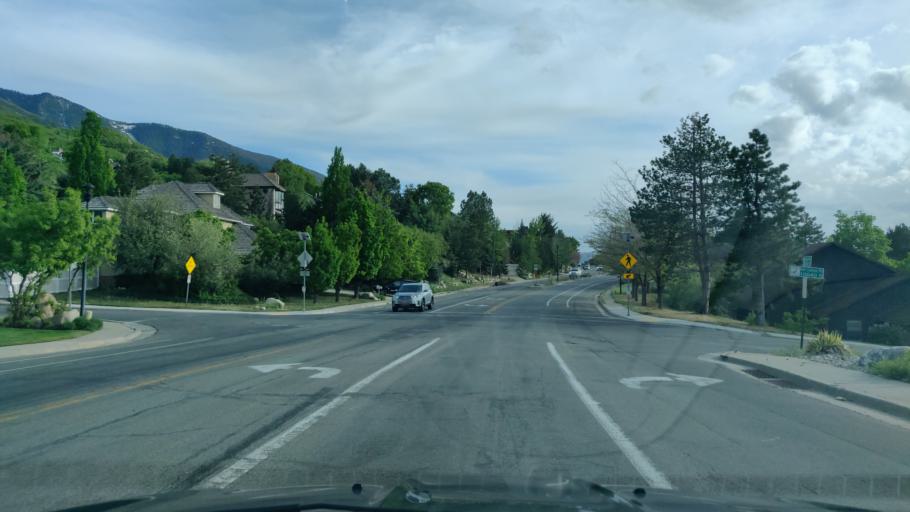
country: US
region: Utah
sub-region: Salt Lake County
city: Granite
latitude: 40.5692
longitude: -111.8016
